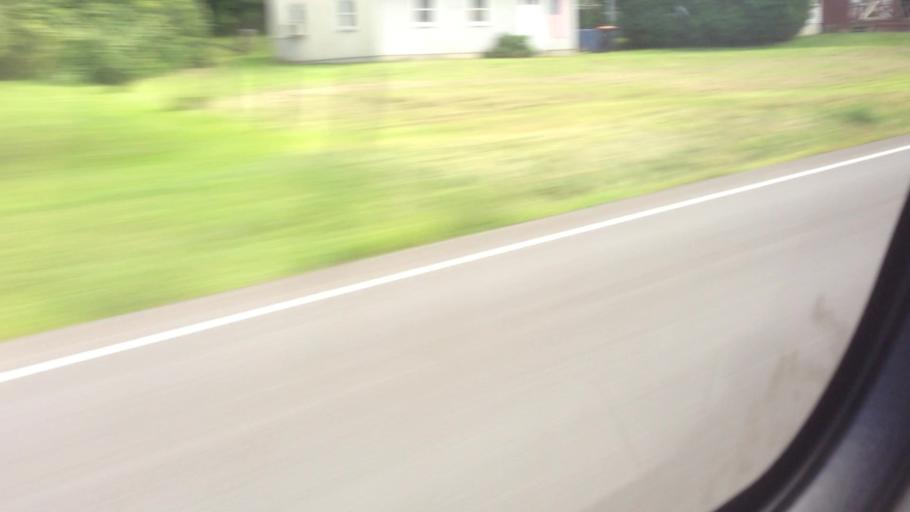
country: US
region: New York
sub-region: Dutchess County
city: Tivoli
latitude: 42.0428
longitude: -73.8951
